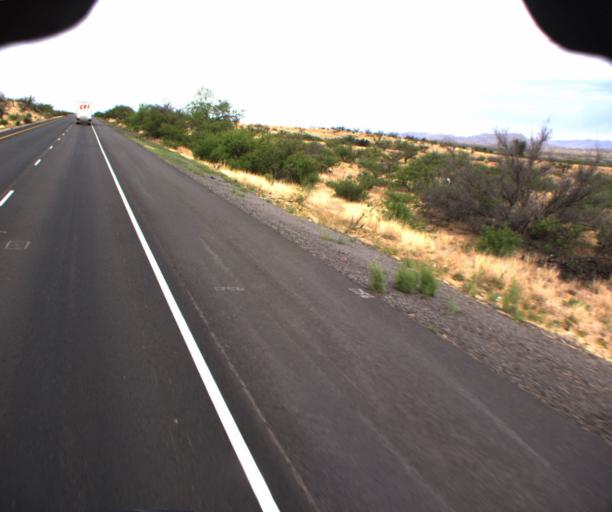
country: US
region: Arizona
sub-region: Cochise County
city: Mescal
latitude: 31.9728
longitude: -110.4868
